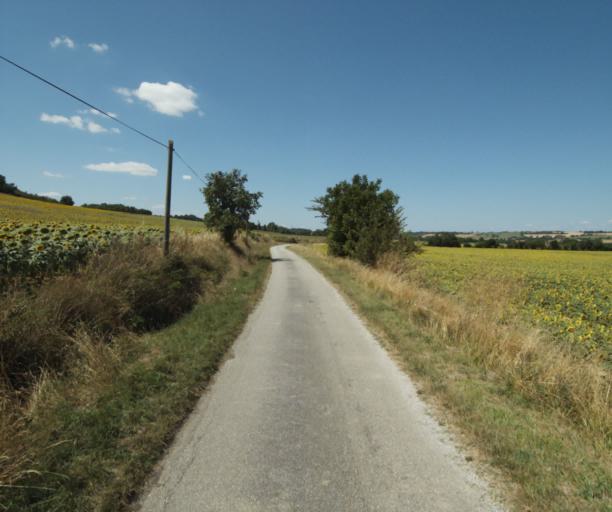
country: FR
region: Midi-Pyrenees
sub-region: Departement de la Haute-Garonne
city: Saint-Felix-Lauragais
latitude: 43.4677
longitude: 1.8870
